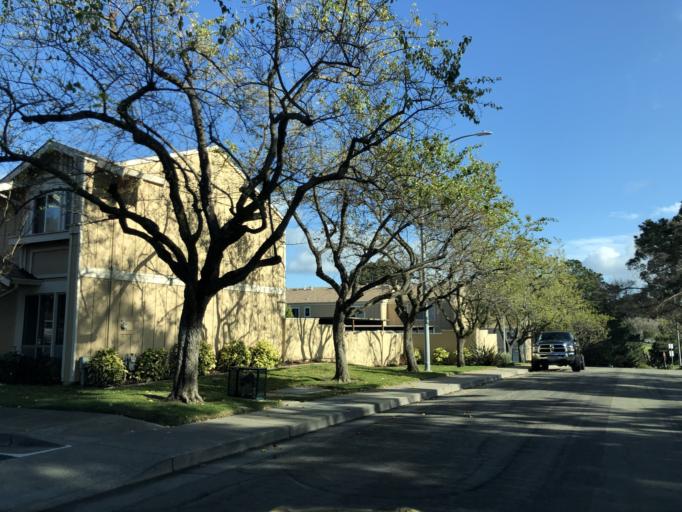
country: US
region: California
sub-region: Contra Costa County
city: Tara Hills
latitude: 37.9824
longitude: -122.3099
